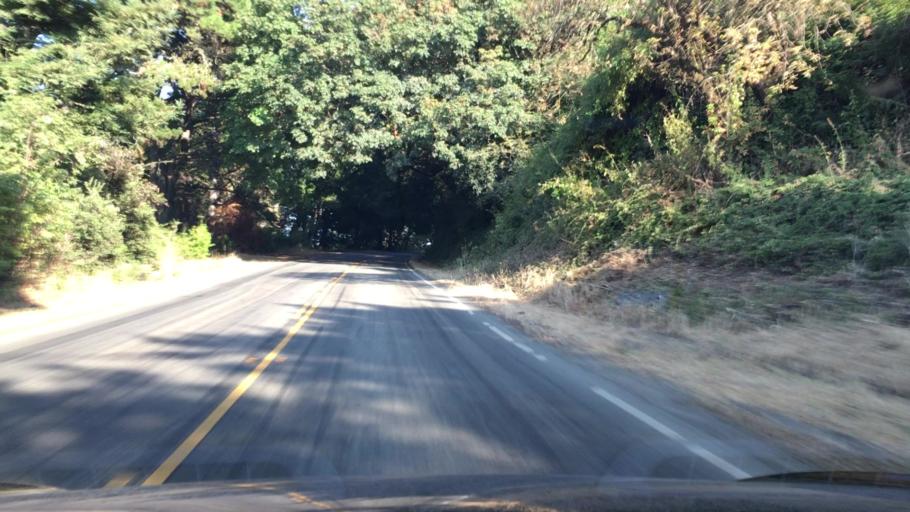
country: US
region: California
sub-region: San Mateo County
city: Portola Valley
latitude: 37.3410
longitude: -122.2196
